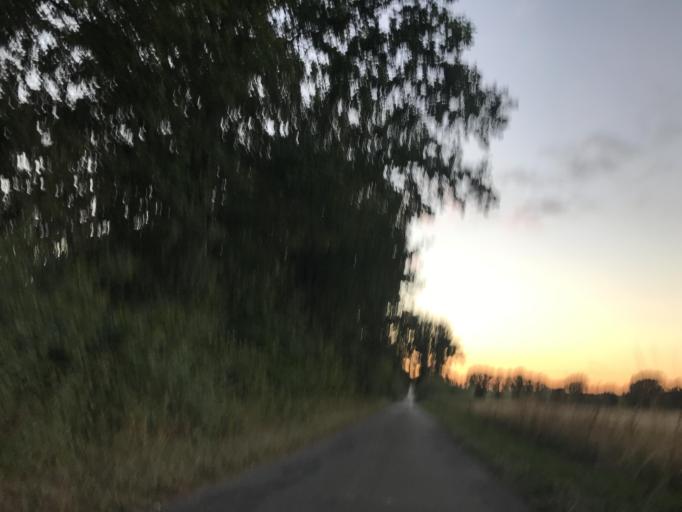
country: DE
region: Lower Saxony
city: Reinstorf
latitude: 53.2281
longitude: 10.5934
